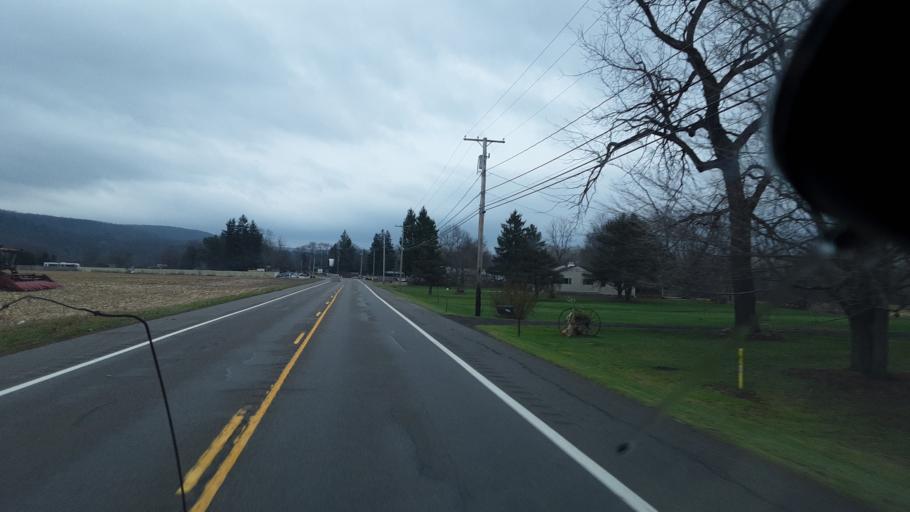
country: US
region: New York
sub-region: Allegany County
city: Belmont
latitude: 42.1975
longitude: -77.9986
